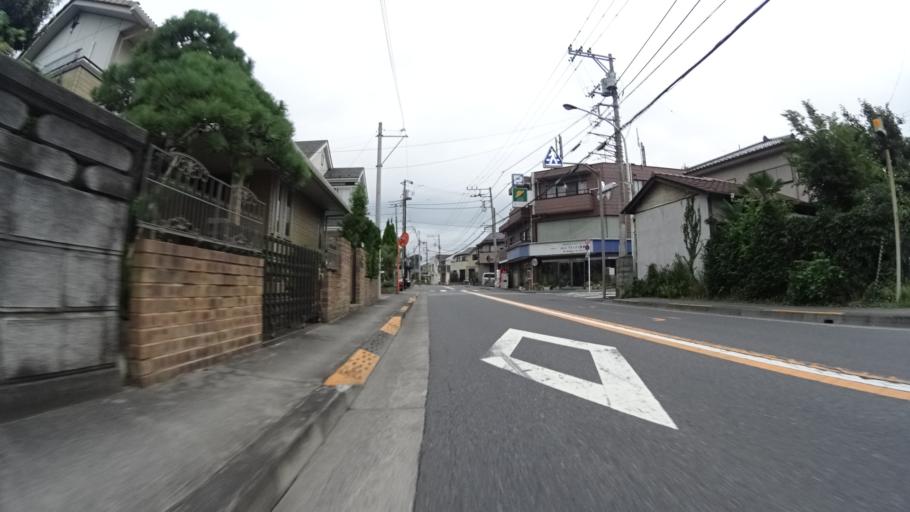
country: JP
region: Tokyo
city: Fussa
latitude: 35.7579
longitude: 139.3076
